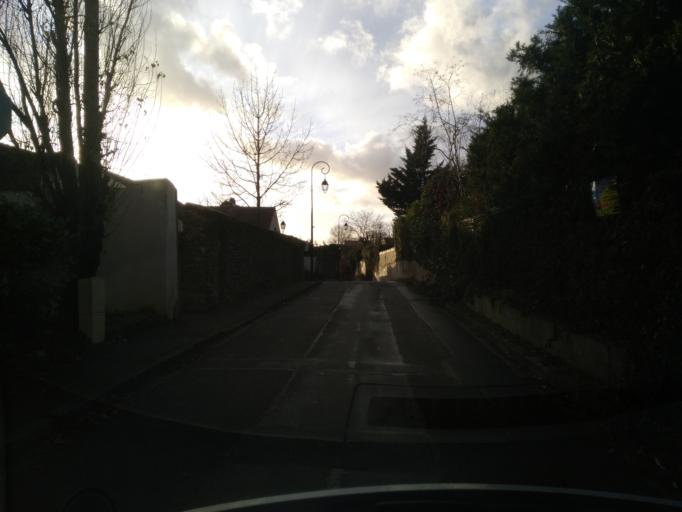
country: FR
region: Ile-de-France
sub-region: Departement des Yvelines
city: Chambourcy
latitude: 48.9004
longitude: 2.0459
